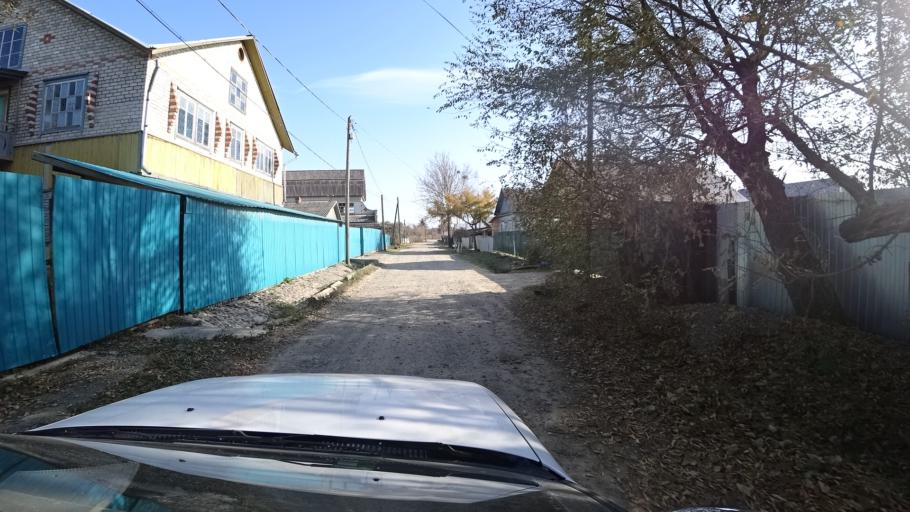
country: RU
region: Primorskiy
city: Dal'nerechensk
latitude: 45.9260
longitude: 133.7250
